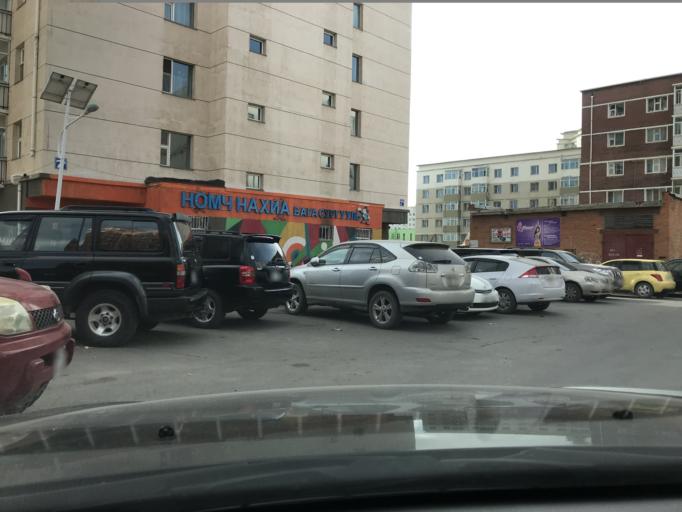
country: MN
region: Ulaanbaatar
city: Ulaanbaatar
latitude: 47.9174
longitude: 106.9415
